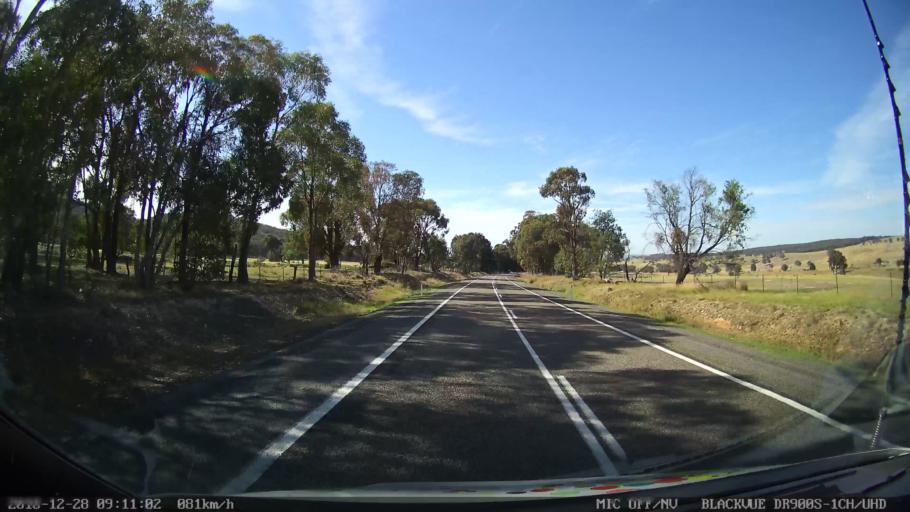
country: AU
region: New South Wales
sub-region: Upper Lachlan Shire
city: Crookwell
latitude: -34.2390
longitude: 149.3380
